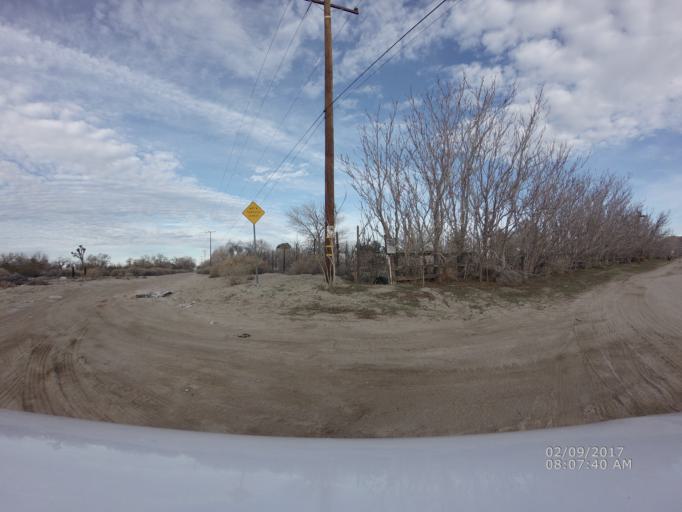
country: US
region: California
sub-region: Los Angeles County
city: Lake Los Angeles
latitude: 34.5726
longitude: -117.8620
